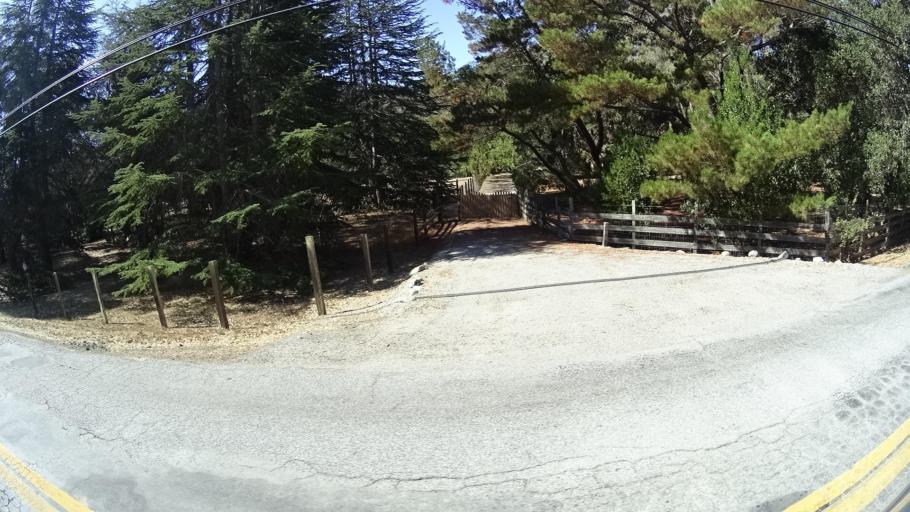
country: US
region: California
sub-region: Monterey County
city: Carmel Valley Village
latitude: 36.5436
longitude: -121.7266
